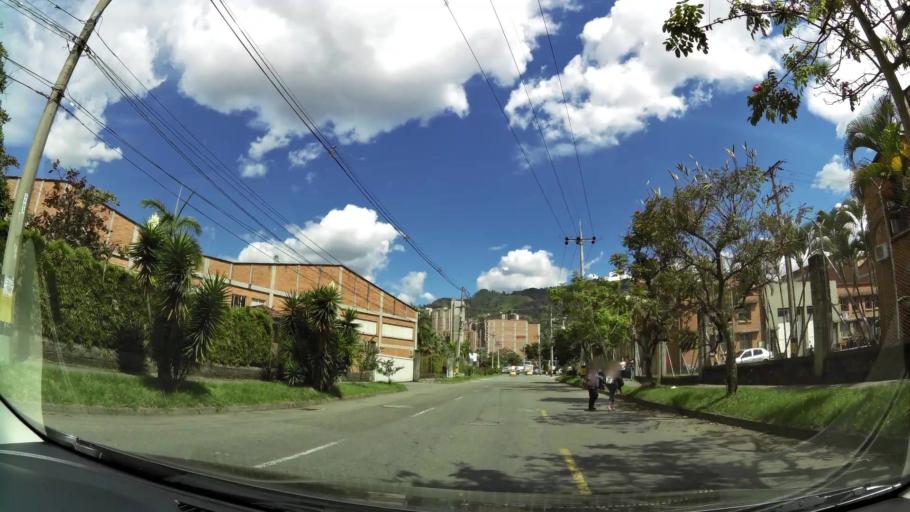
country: CO
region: Antioquia
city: Sabaneta
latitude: 6.1572
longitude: -75.6129
